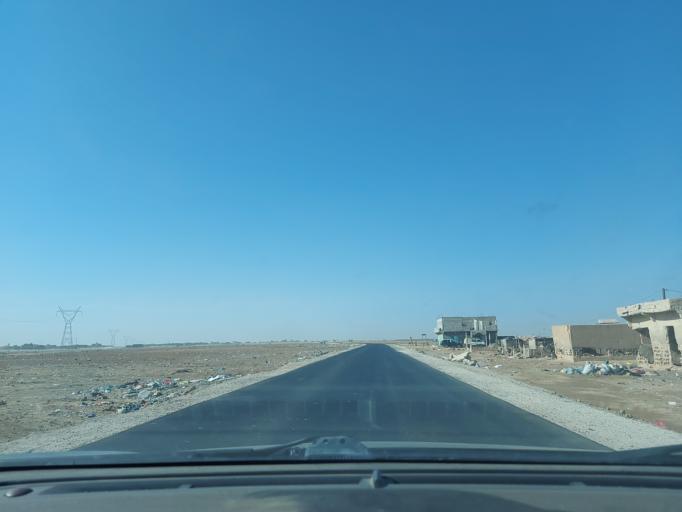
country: MR
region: Nouakchott
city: Nouakchott
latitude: 18.0087
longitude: -15.9877
